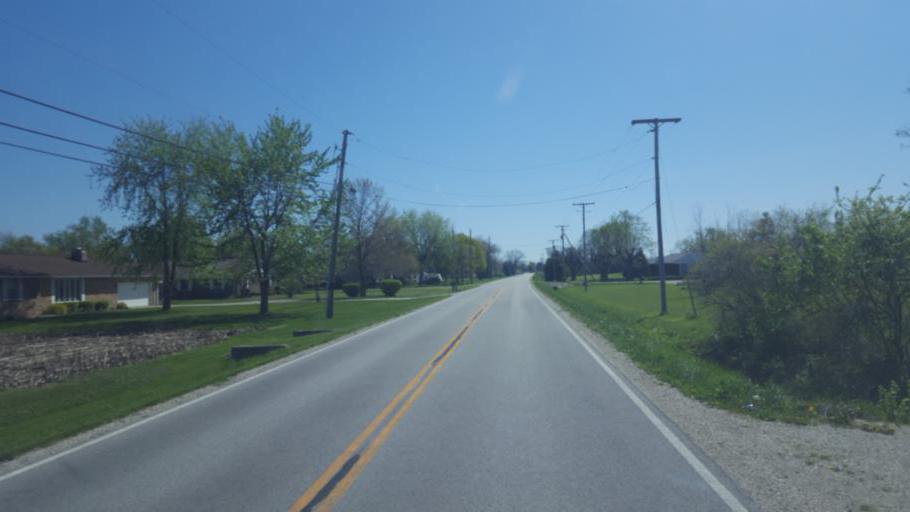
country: US
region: Ohio
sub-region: Sandusky County
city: Stony Prairie
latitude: 41.3281
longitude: -83.1795
